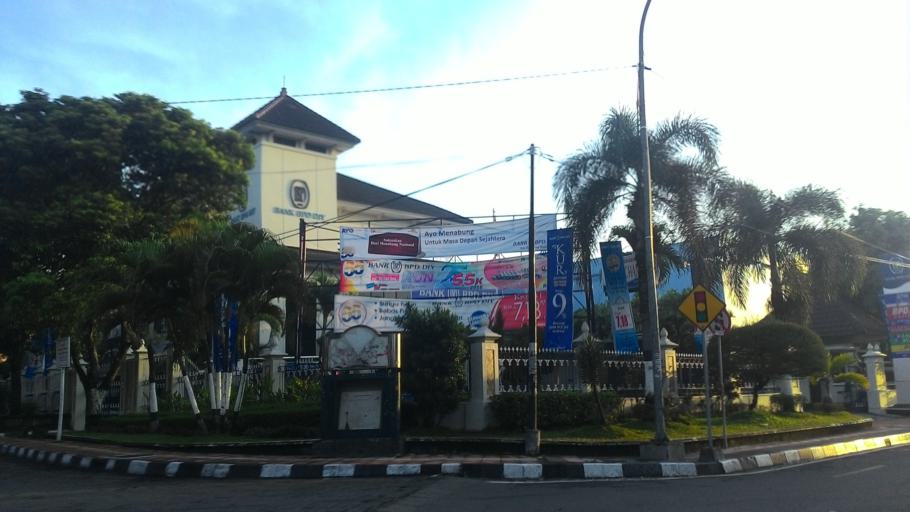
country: ID
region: Daerah Istimewa Yogyakarta
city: Yogyakarta
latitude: -7.8015
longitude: 110.3682
